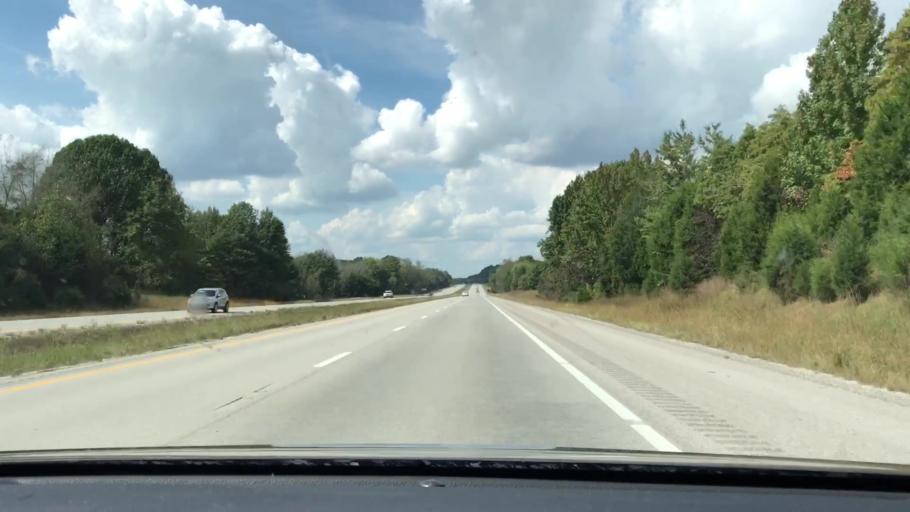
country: US
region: Kentucky
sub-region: Barren County
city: Cave City
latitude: 37.0314
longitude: -86.0512
